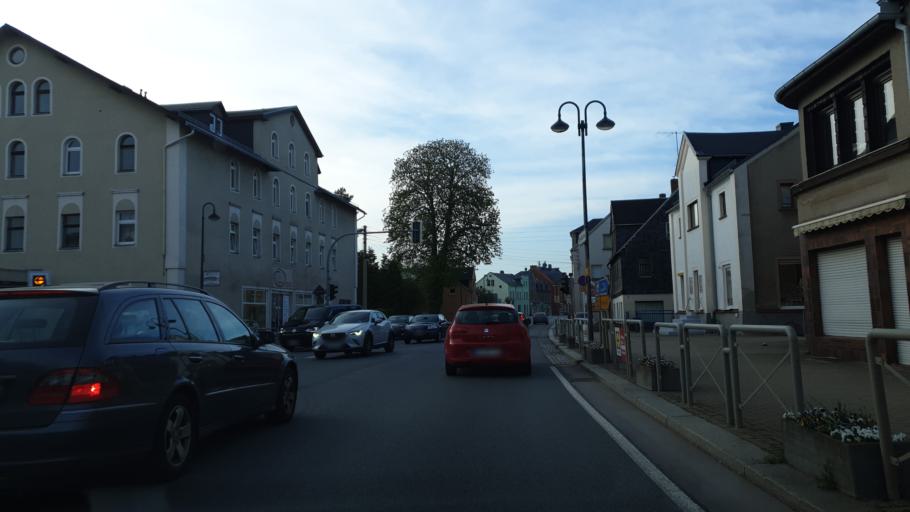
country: DE
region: Saxony
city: Lugau
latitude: 50.7373
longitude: 12.7470
